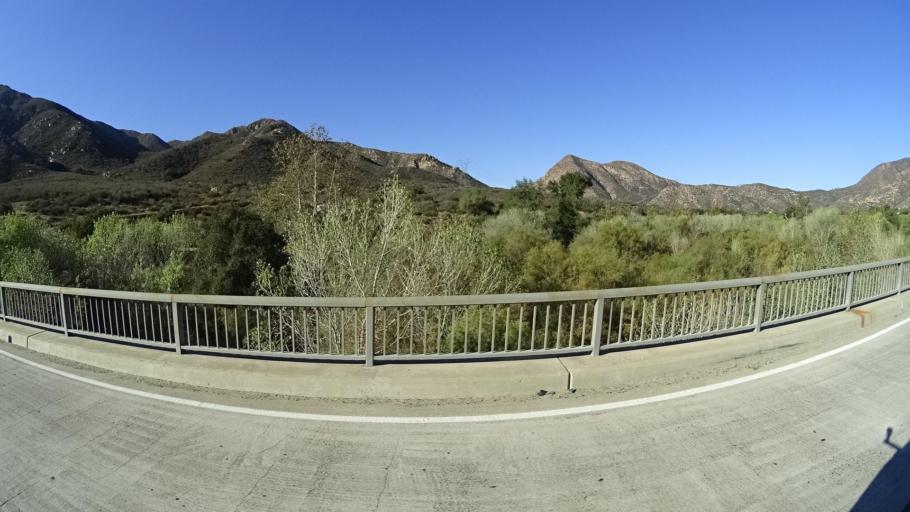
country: MX
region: Baja California
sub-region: Tecate
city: Lomas de Santa Anita
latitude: 32.6084
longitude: -116.7001
